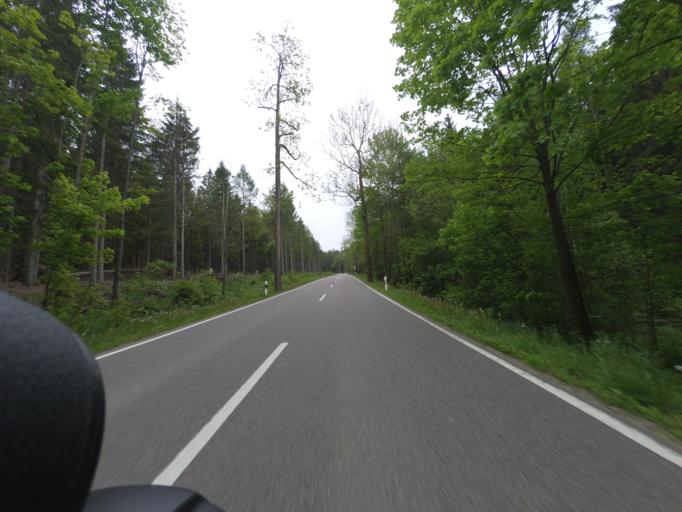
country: DE
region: Saxony
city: Bornichen
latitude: 50.7404
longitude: 13.1479
